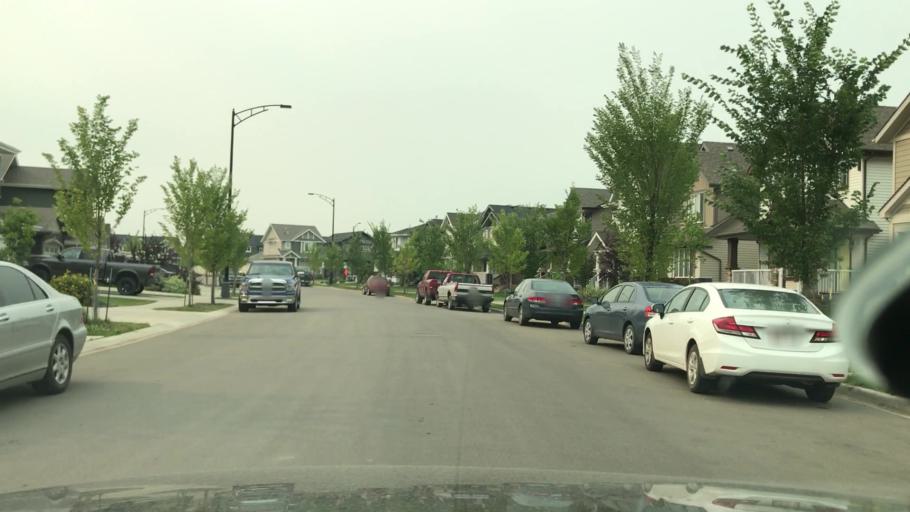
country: CA
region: Alberta
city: Devon
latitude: 53.4229
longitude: -113.5973
